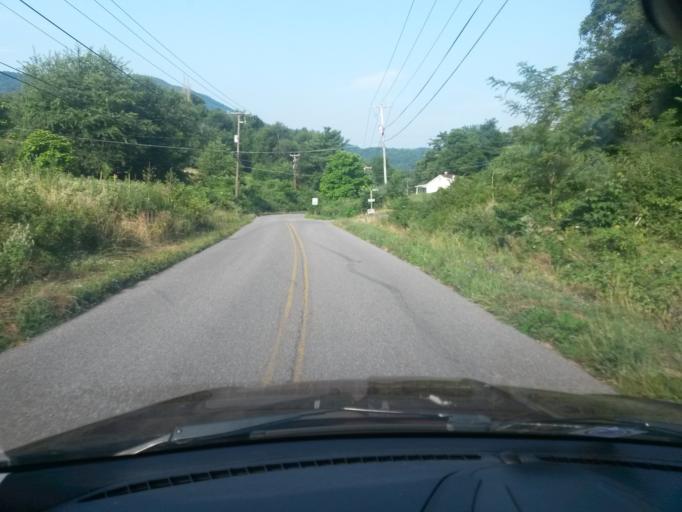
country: US
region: Virginia
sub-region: Giles County
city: Narrows
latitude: 37.3689
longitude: -80.8092
